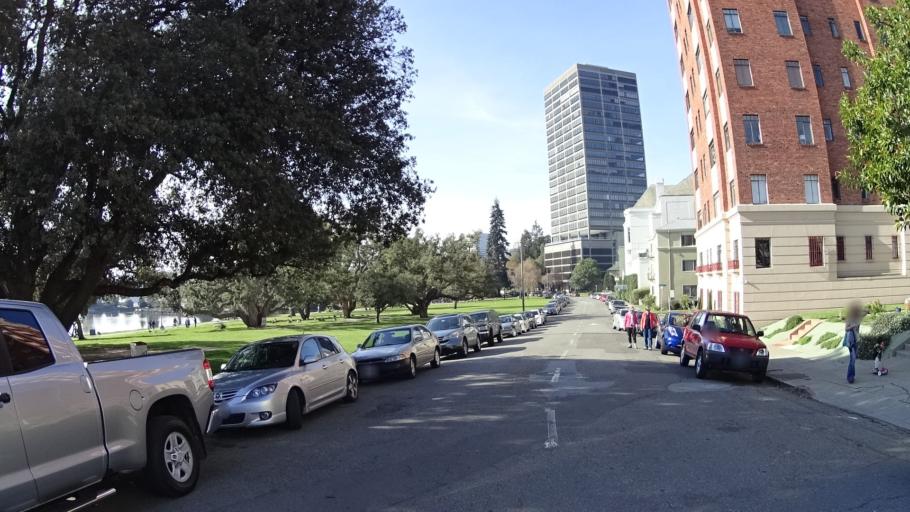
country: US
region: California
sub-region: Alameda County
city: Oakland
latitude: 37.8077
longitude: -122.2534
